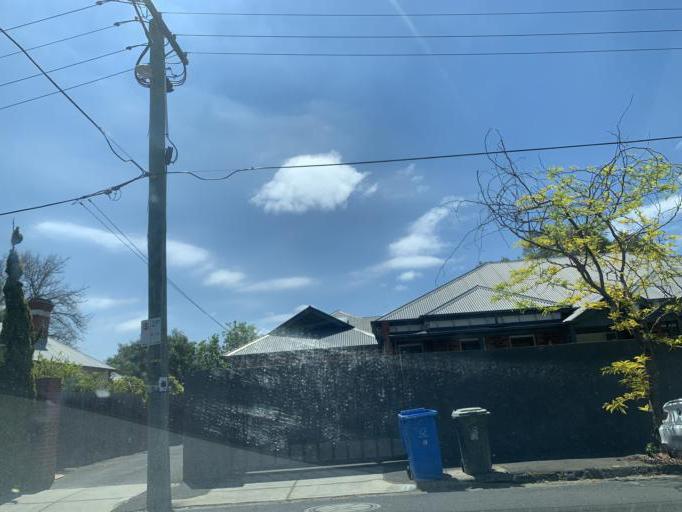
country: AU
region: Victoria
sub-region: Bayside
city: North Brighton
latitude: -37.9037
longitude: 145.0004
